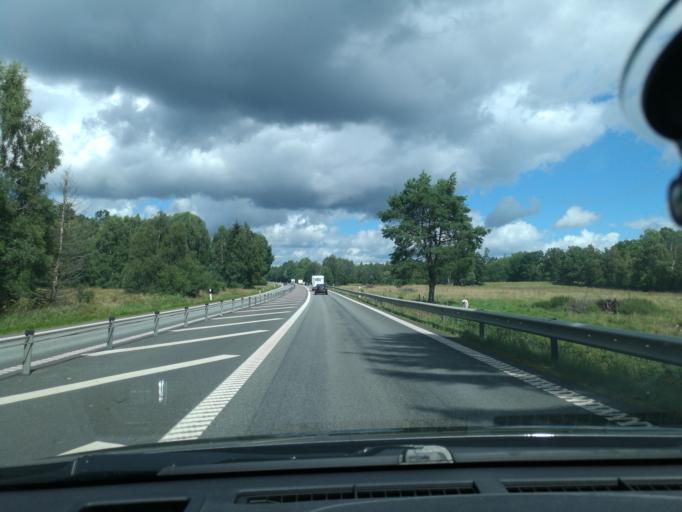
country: SE
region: Skane
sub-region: Osby Kommun
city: Osby
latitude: 56.3739
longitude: 14.0335
